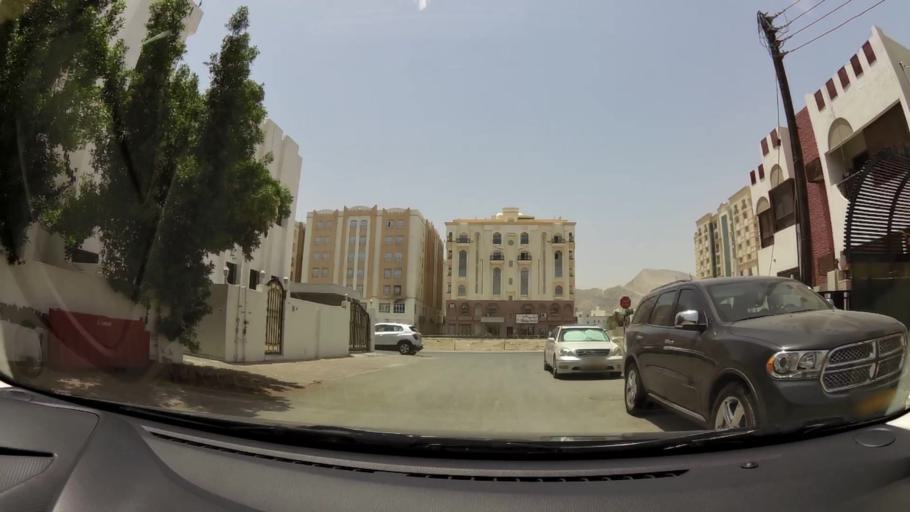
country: OM
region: Muhafazat Masqat
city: Bawshar
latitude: 23.5845
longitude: 58.4241
